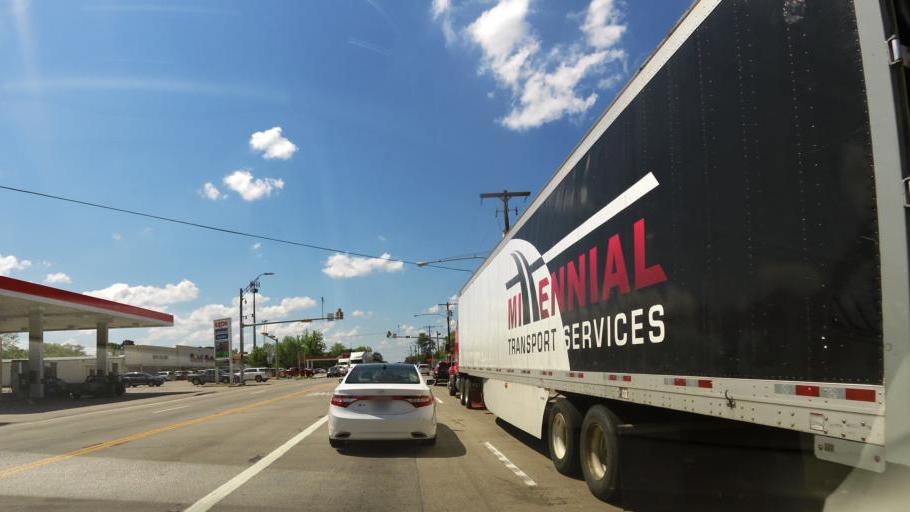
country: US
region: Texas
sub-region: Polk County
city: Corrigan
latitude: 30.9974
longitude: -94.8274
